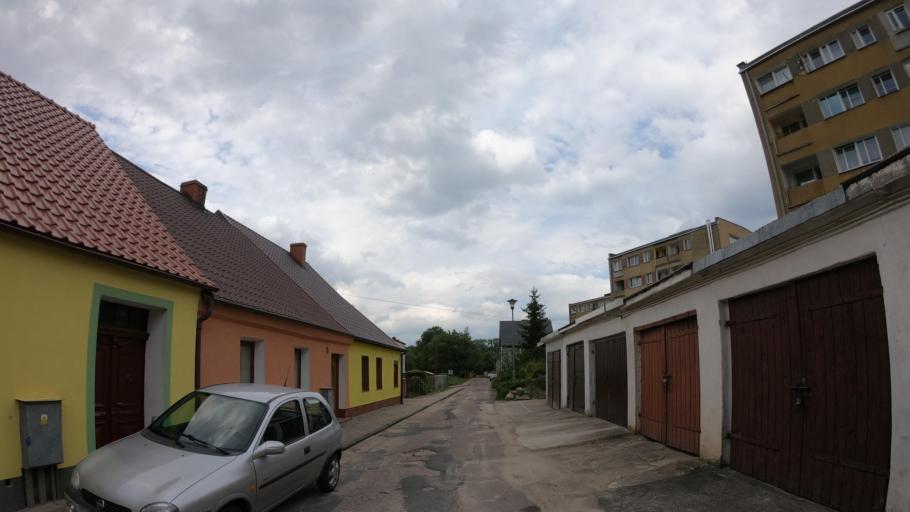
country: PL
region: West Pomeranian Voivodeship
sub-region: Powiat drawski
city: Kalisz Pomorski
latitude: 53.2979
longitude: 15.9037
